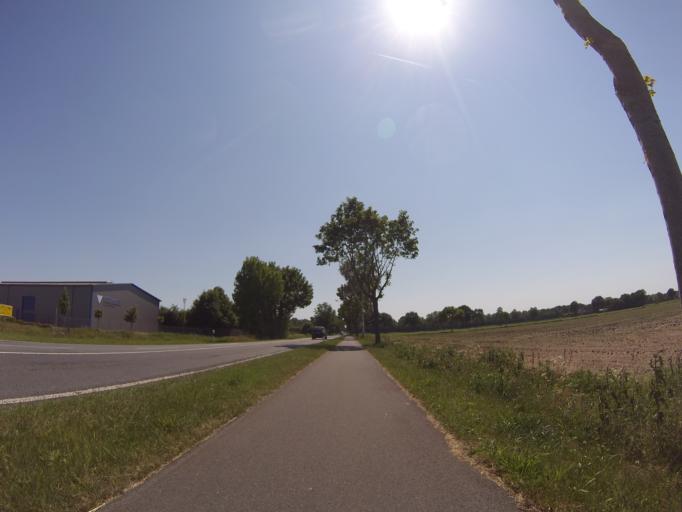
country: DE
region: Lower Saxony
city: Emlichheim
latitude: 52.6245
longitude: 6.8579
